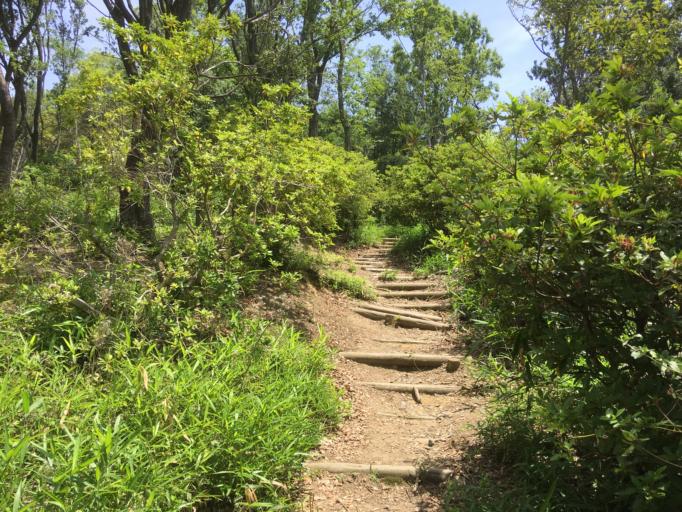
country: JP
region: Nara
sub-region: Ikoma-shi
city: Ikoma
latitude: 34.6667
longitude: 135.6591
